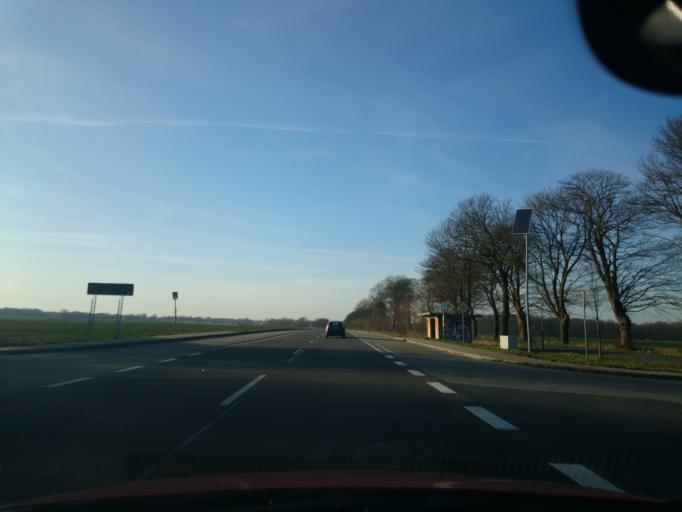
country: DE
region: Mecklenburg-Vorpommern
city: Mesekenhagen
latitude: 54.1949
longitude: 13.2689
